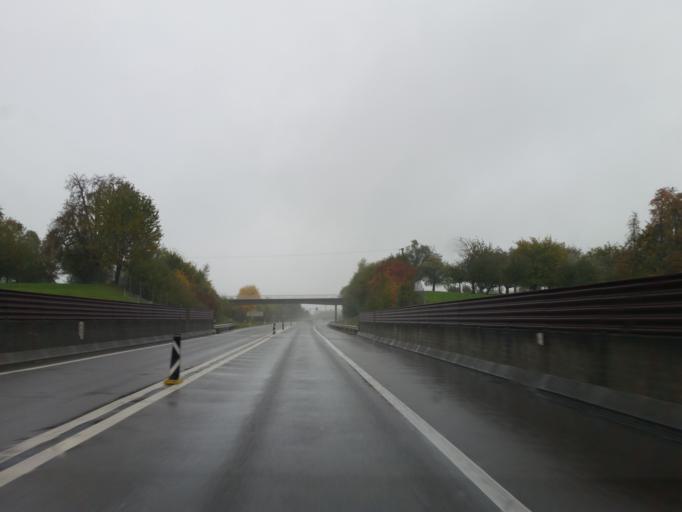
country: CH
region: Saint Gallen
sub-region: Wahlkreis Rorschach
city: Morschwil
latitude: 47.4883
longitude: 9.4343
